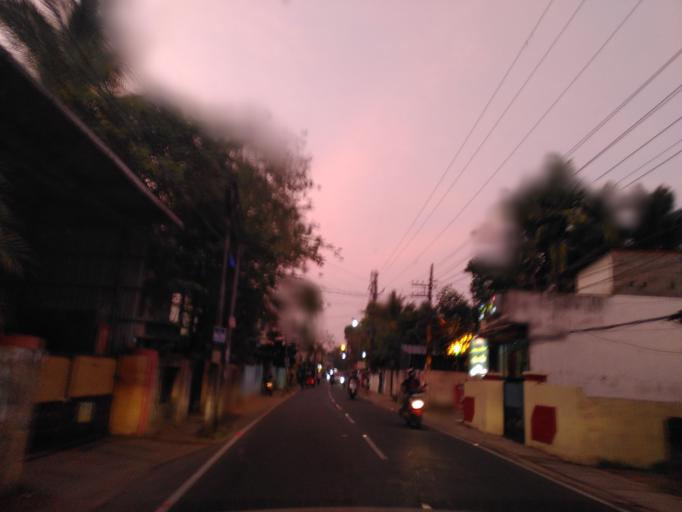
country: IN
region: Kerala
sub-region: Ernakulam
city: Cochin
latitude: 9.9116
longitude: 76.2795
